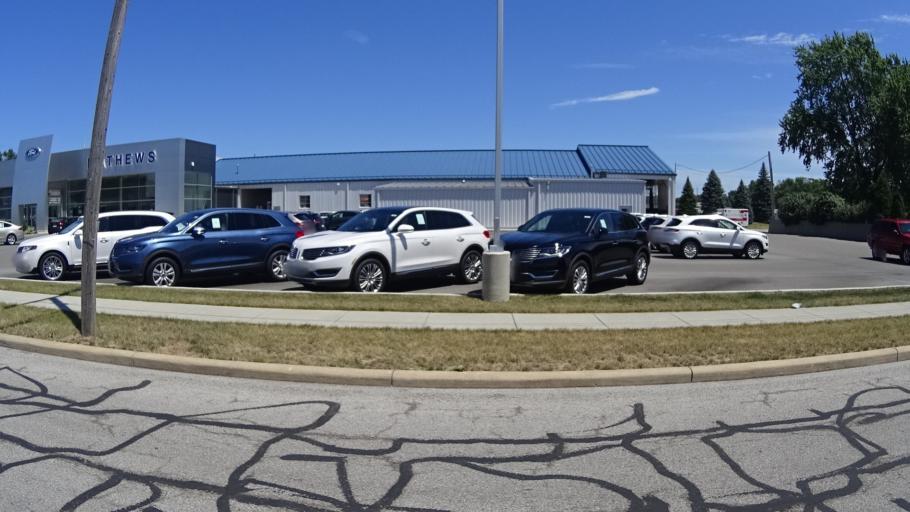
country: US
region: Ohio
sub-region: Erie County
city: Sandusky
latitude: 41.4321
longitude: -82.6910
